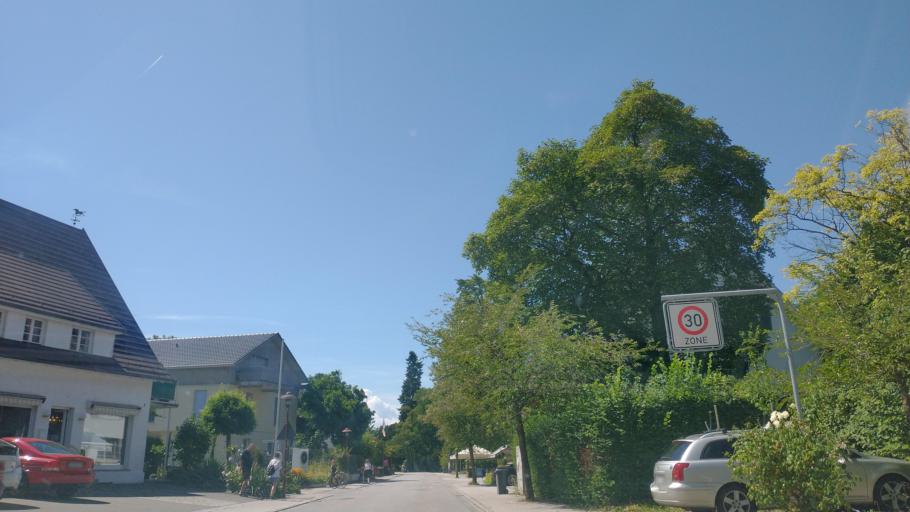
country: DE
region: Baden-Wuerttemberg
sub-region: Tuebingen Region
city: Kressbronn am Bodensee
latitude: 47.5926
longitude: 9.6007
